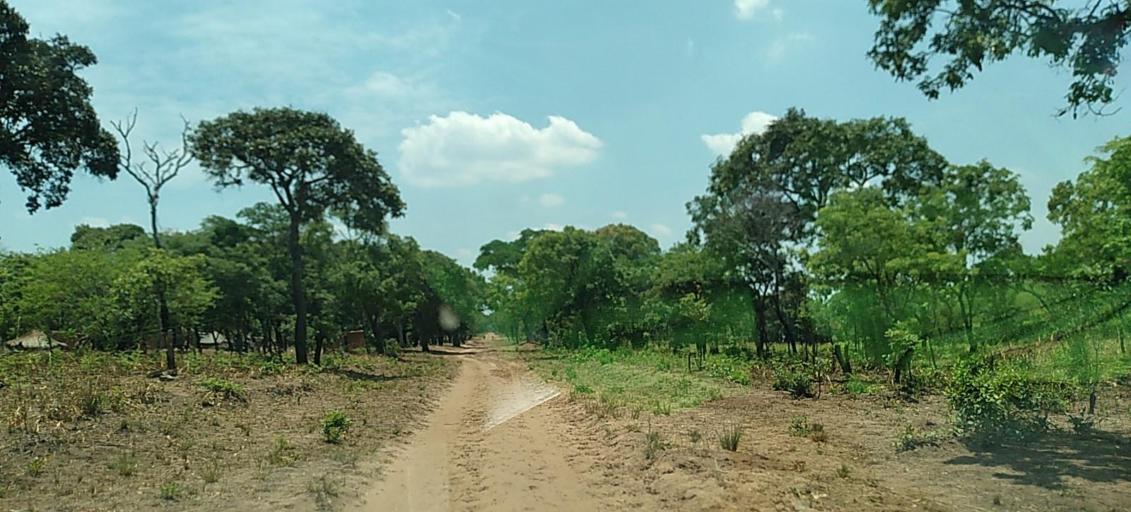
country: CD
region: Katanga
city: Kolwezi
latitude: -11.4738
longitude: 25.2317
